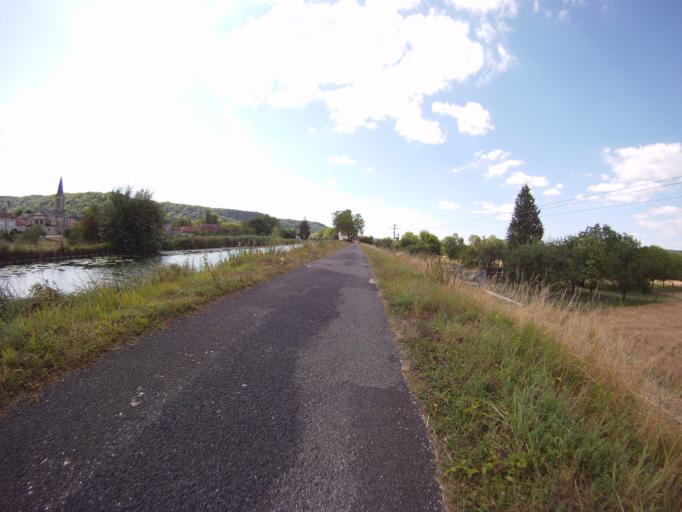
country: FR
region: Lorraine
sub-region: Departement de la Meuse
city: Longeville-en-Barrois
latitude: 48.7262
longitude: 5.2350
